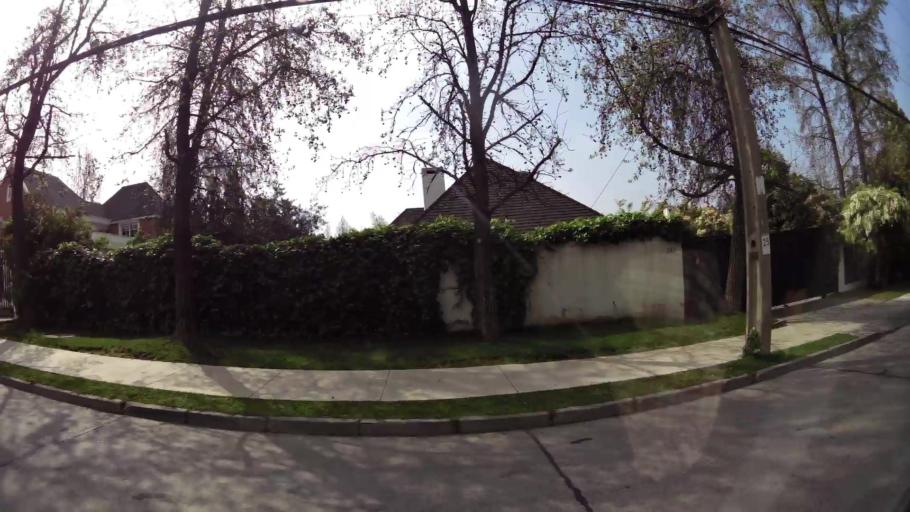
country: CL
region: Santiago Metropolitan
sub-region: Provincia de Santiago
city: Villa Presidente Frei, Nunoa, Santiago, Chile
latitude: -33.3735
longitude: -70.5840
